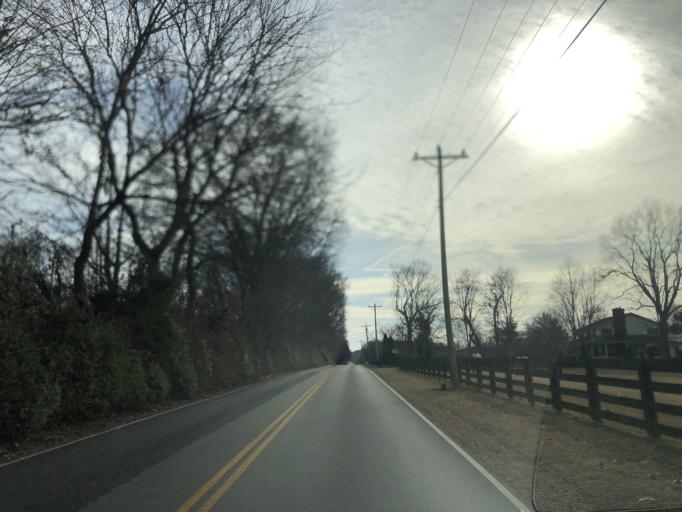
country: US
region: Tennessee
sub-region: Williamson County
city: Franklin
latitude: 35.9532
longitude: -86.9019
